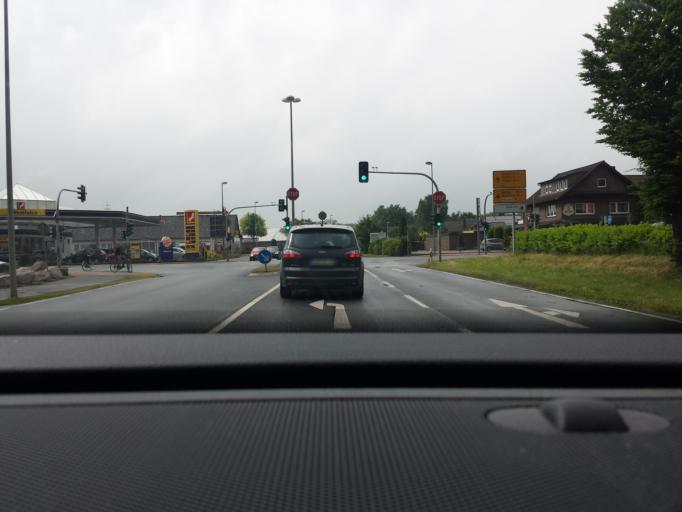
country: DE
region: North Rhine-Westphalia
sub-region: Regierungsbezirk Munster
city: Ahaus
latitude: 52.0734
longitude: 6.9978
